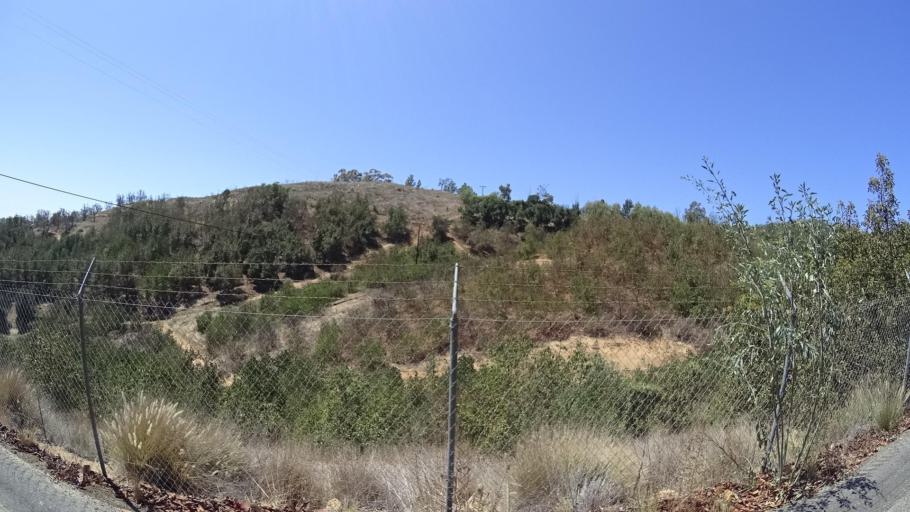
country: US
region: California
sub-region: San Diego County
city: Hidden Meadows
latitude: 33.3059
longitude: -117.0918
